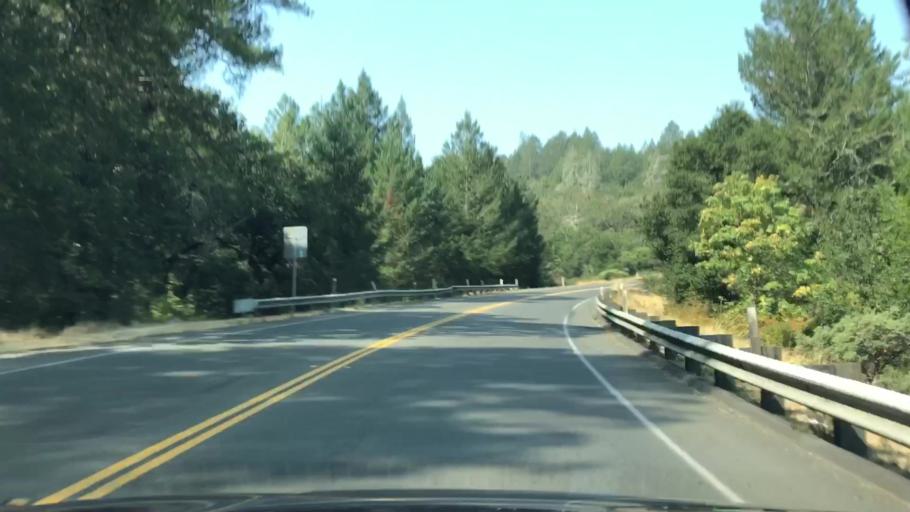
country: US
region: California
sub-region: Napa County
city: Calistoga
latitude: 38.5775
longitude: -122.6072
